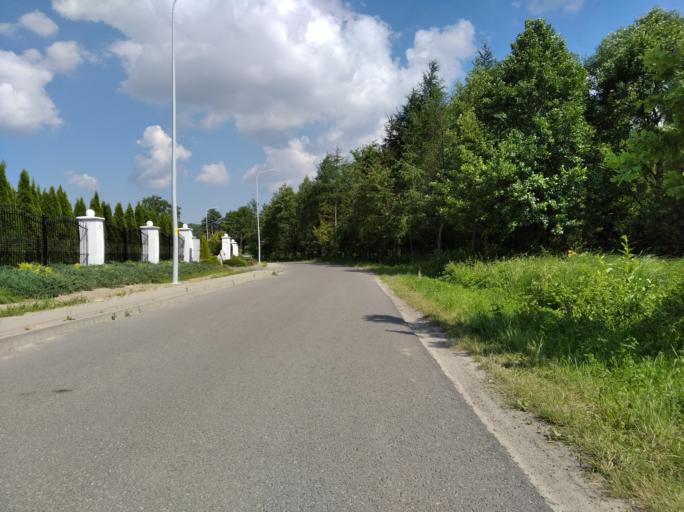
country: PL
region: Subcarpathian Voivodeship
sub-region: Powiat rzeszowski
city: Dynow
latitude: 49.8327
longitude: 22.2243
